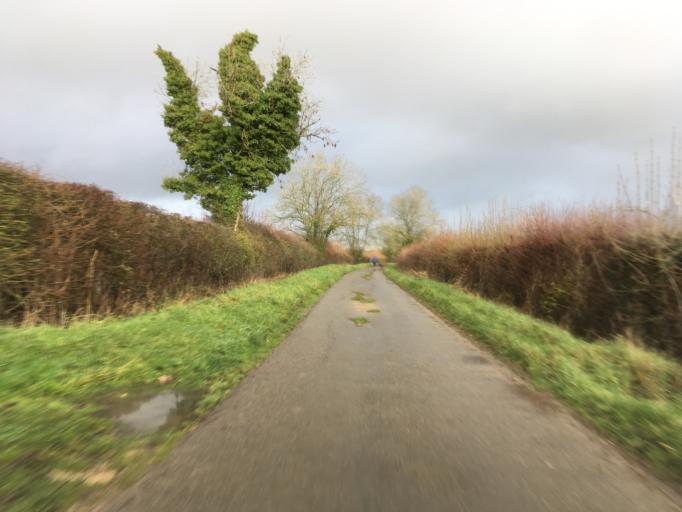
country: GB
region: England
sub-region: Wiltshire
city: Hankerton
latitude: 51.6453
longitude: -2.0738
